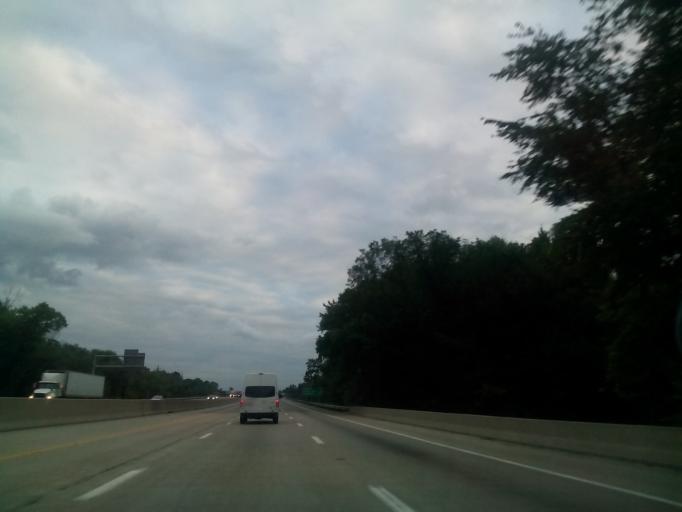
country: US
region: Ohio
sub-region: Trumbull County
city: Newton Falls
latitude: 41.2091
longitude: -80.9492
